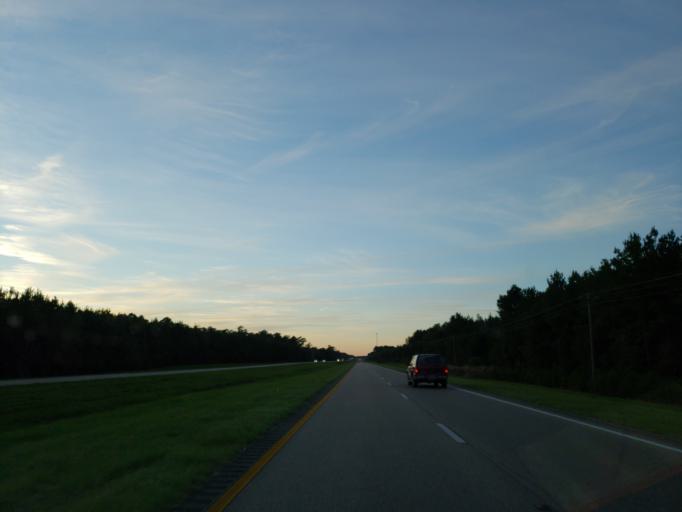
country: US
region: Mississippi
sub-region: Wayne County
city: Belmont
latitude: 31.6036
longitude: -88.5600
